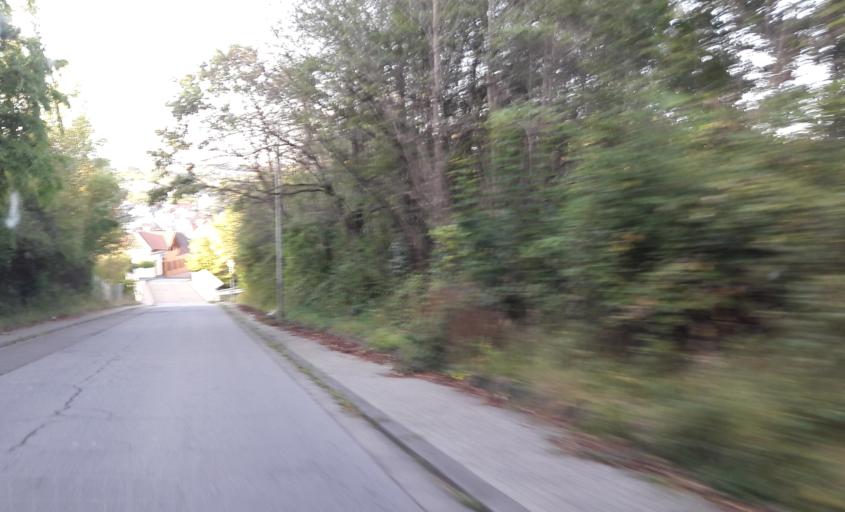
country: DE
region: Saarland
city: Schiffweiler
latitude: 49.3527
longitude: 7.1312
